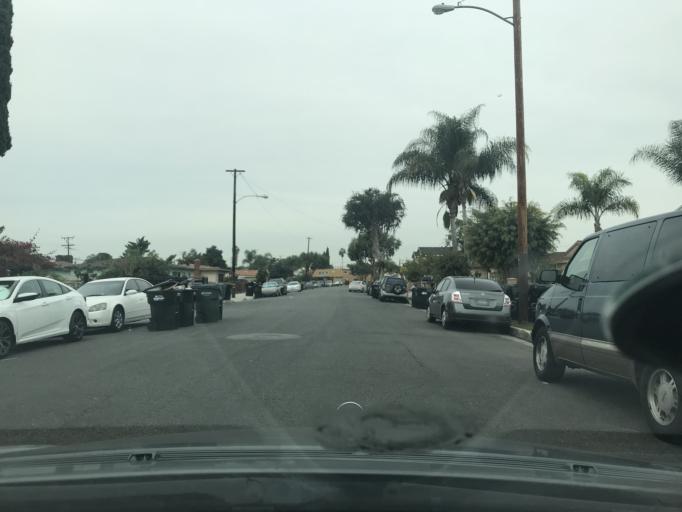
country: US
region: California
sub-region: Los Angeles County
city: Bell Gardens
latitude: 33.9617
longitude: -118.1604
